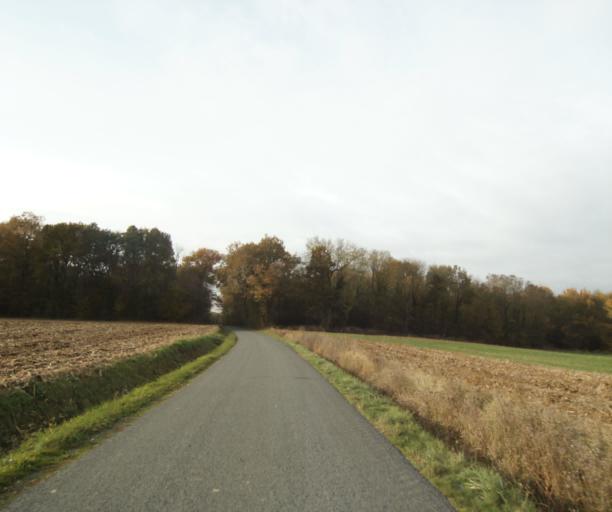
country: FR
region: Poitou-Charentes
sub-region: Departement de la Charente-Maritime
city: Nieul-les-Saintes
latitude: 45.7767
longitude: -0.7315
